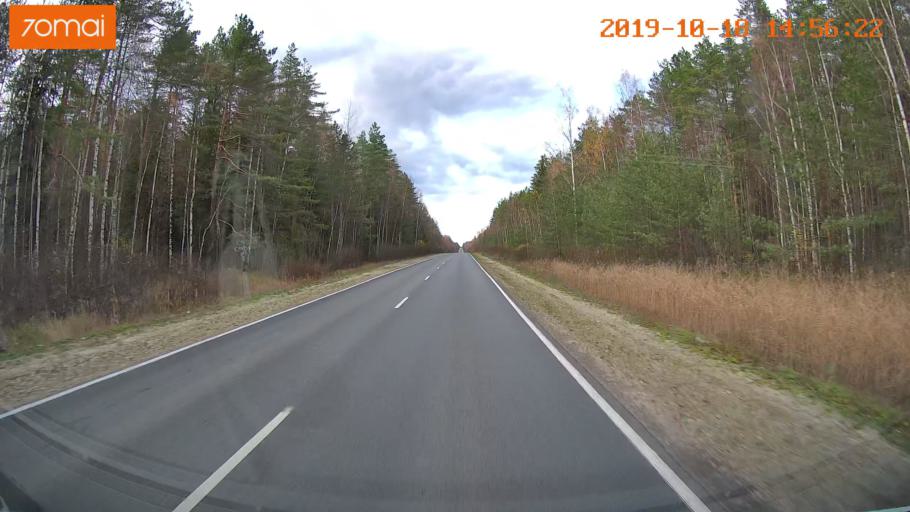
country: RU
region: Vladimir
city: Kurlovo
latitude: 55.4636
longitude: 40.5879
